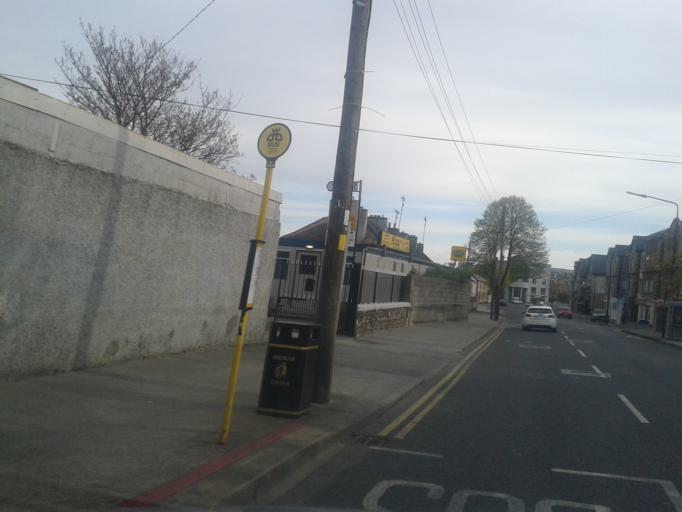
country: IE
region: Leinster
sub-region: Fingal County
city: Swords
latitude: 53.4611
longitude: -6.2187
